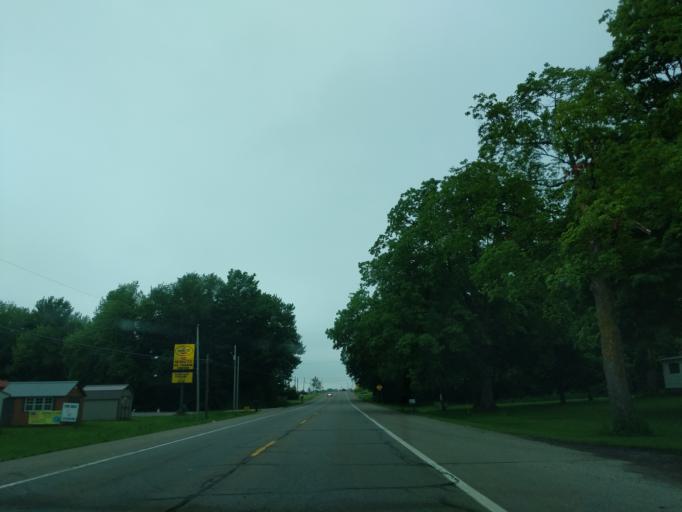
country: US
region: Michigan
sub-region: Branch County
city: Coldwater
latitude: 41.9382
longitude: -84.9498
